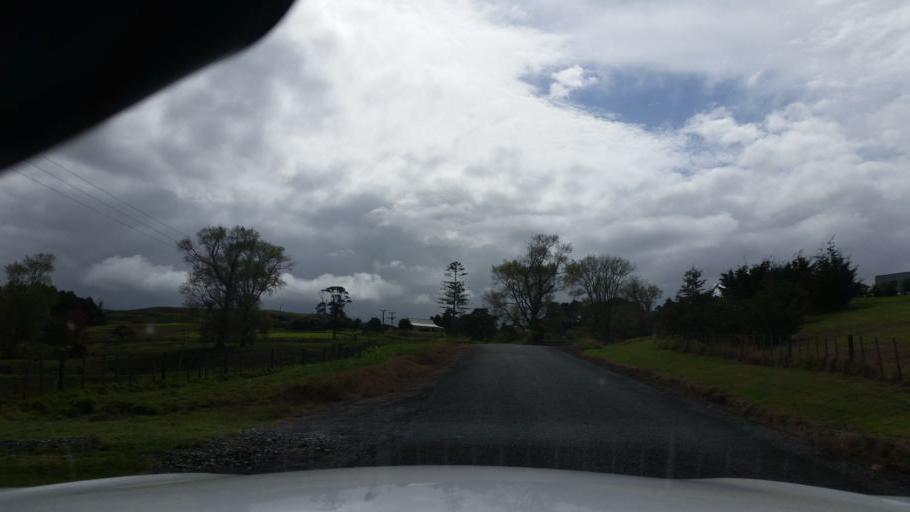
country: NZ
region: Northland
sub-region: Whangarei
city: Ruakaka
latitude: -36.1084
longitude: 174.2772
